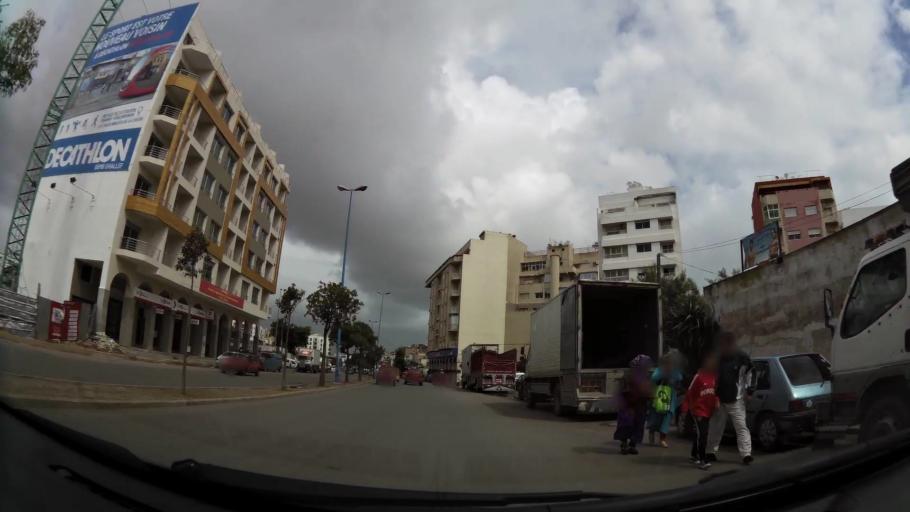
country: MA
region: Grand Casablanca
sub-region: Casablanca
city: Casablanca
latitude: 33.5743
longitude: -7.6318
